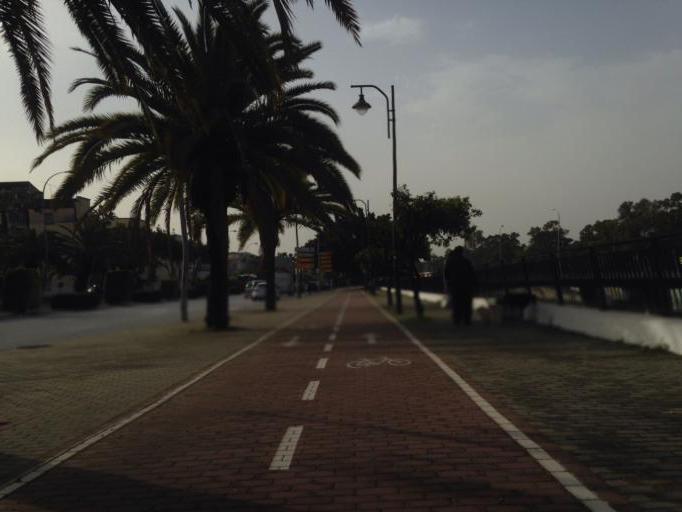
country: ES
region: Andalusia
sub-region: Provincia de Malaga
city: Malaga
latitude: 36.7341
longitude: -4.4252
